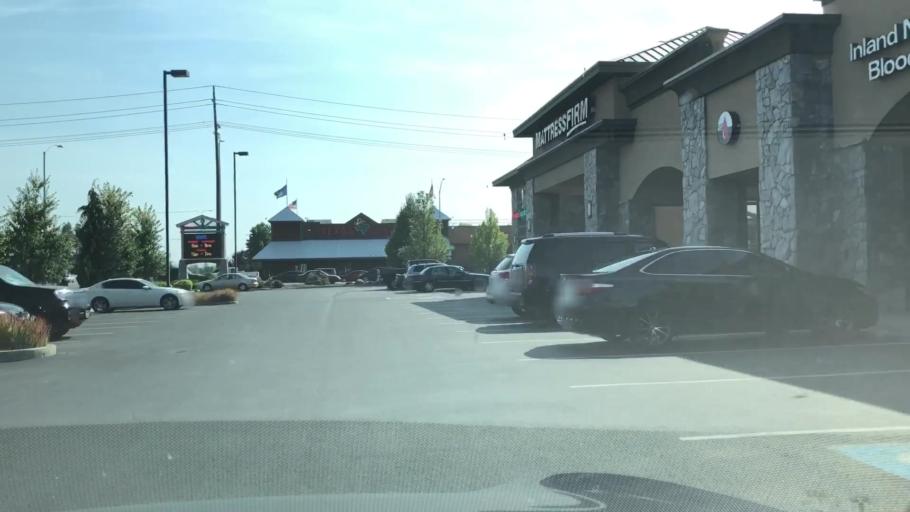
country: US
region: Idaho
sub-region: Kootenai County
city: Dalton Gardens
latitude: 47.7081
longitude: -116.7921
